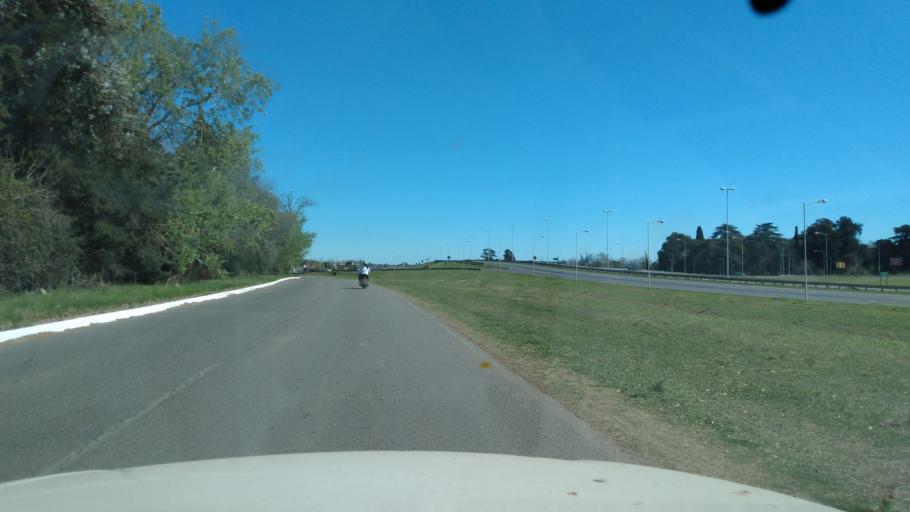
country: AR
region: Buenos Aires
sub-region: Partido de Lujan
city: Lujan
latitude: -34.5580
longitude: -59.0970
